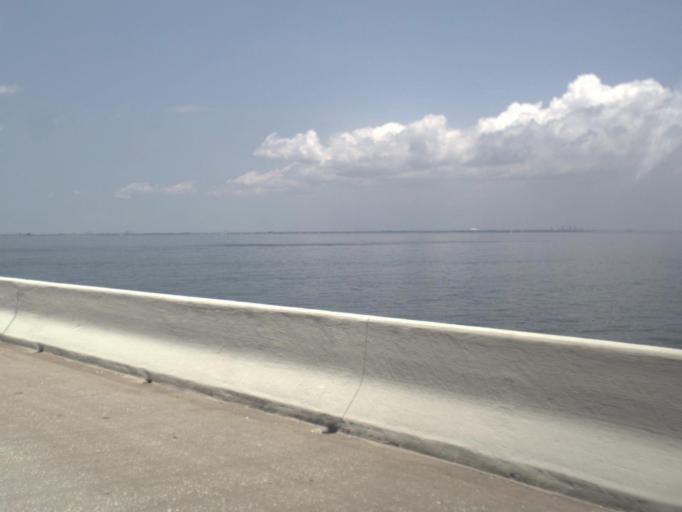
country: US
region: Florida
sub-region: Manatee County
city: Memphis
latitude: 27.5939
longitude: -82.6319
